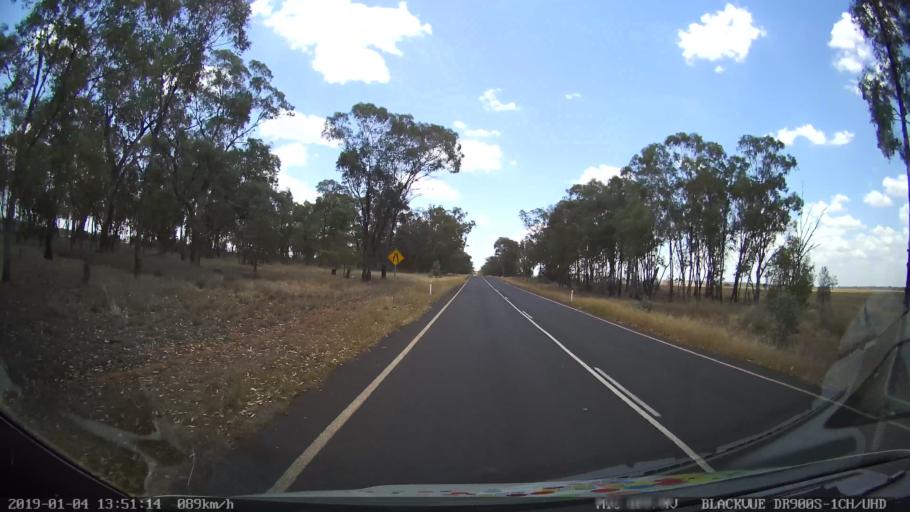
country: AU
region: New South Wales
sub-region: Dubbo Municipality
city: Dubbo
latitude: -32.4098
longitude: 148.5709
